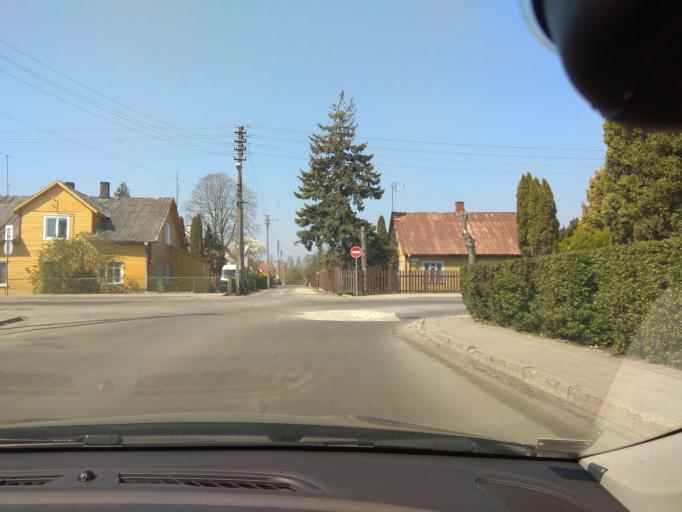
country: LT
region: Marijampoles apskritis
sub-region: Marijampole Municipality
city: Marijampole
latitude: 54.5643
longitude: 23.3501
